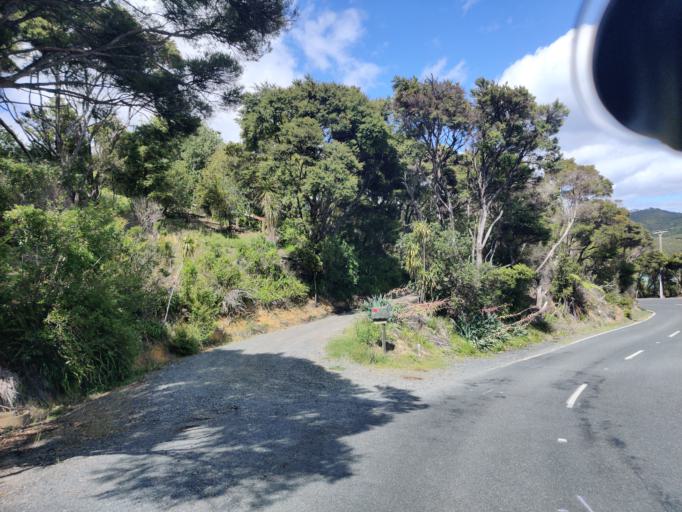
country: NZ
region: Northland
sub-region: Far North District
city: Paihia
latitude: -35.2572
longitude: 174.2347
